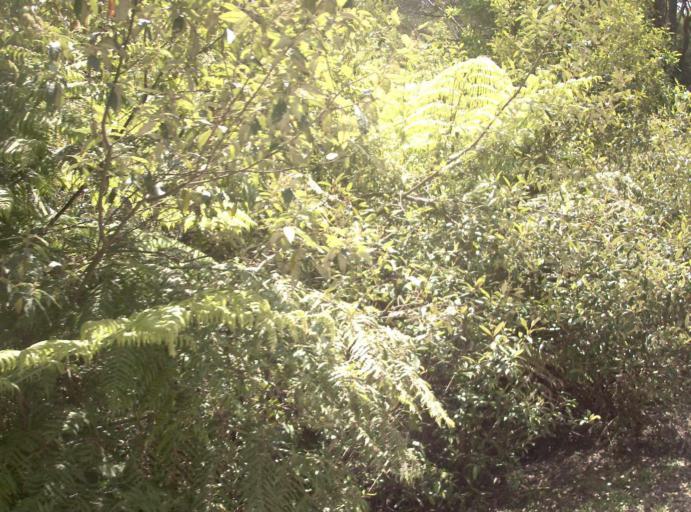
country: AU
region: Victoria
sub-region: Latrobe
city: Morwell
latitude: -38.4361
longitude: 146.5271
